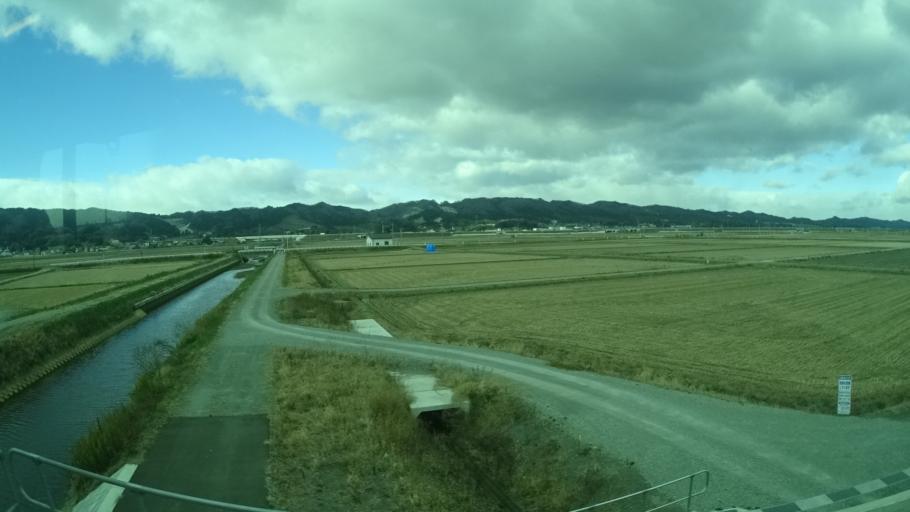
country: JP
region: Miyagi
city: Watari
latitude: 37.9790
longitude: 140.8871
